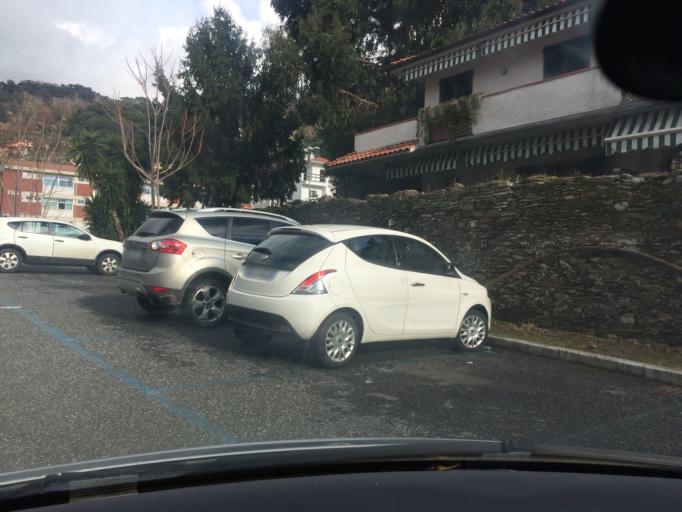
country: IT
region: Tuscany
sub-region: Provincia di Massa-Carrara
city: Massa
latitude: 44.0400
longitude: 10.1434
